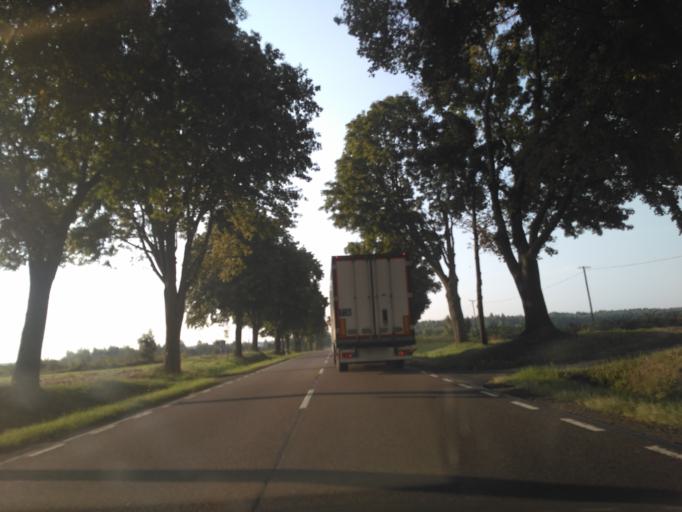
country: PL
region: Lublin Voivodeship
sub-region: Powiat krasnicki
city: Krasnik
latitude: 50.8789
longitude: 22.2636
